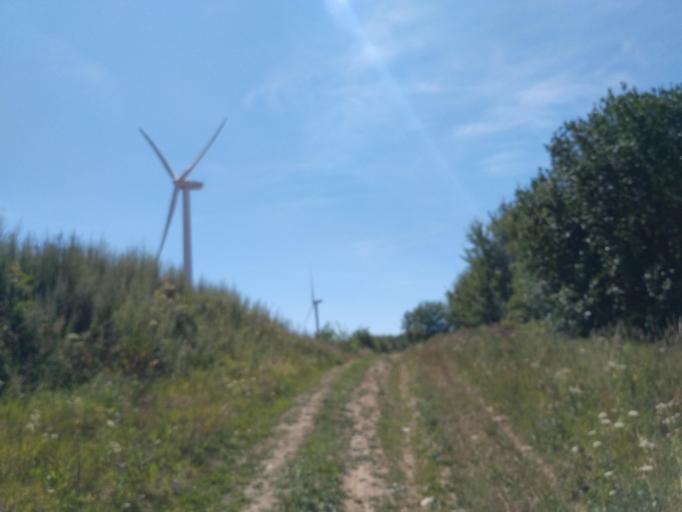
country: PL
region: Subcarpathian Voivodeship
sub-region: Powiat sanocki
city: Bukowsko
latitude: 49.5110
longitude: 22.0552
